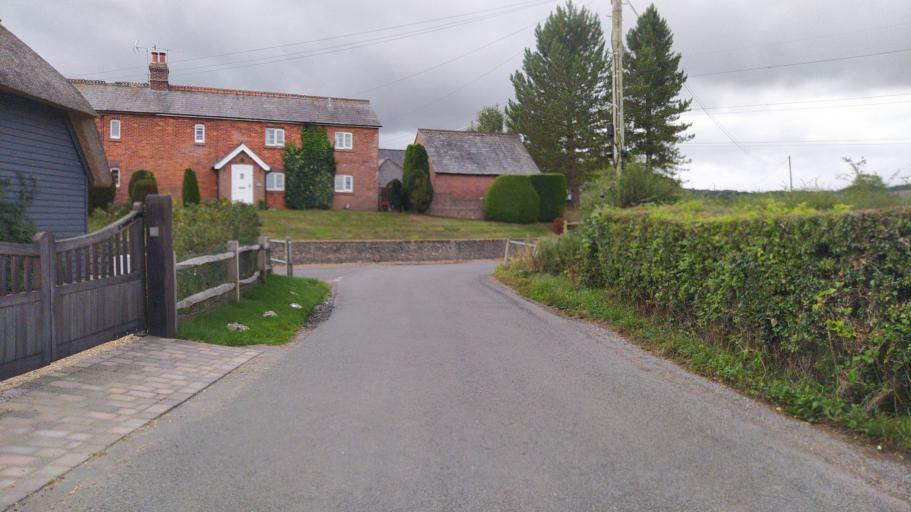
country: GB
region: England
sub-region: Hampshire
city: Petersfield
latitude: 50.9856
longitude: -1.0156
